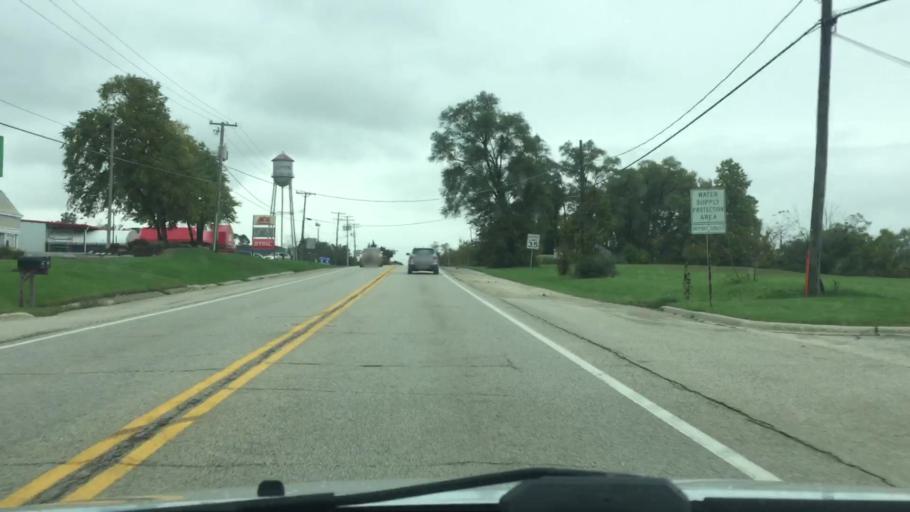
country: US
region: Illinois
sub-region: McHenry County
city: Richmond
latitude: 42.4852
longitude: -88.3061
